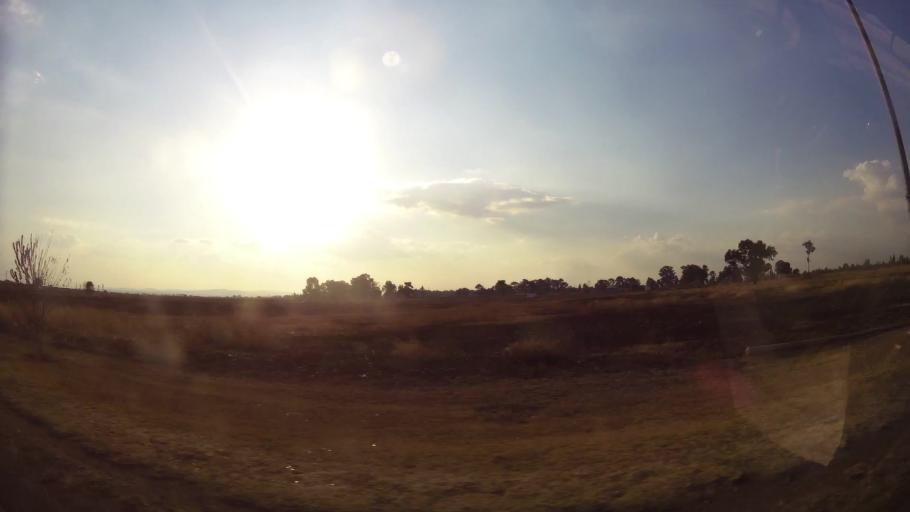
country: ZA
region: Gauteng
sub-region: Ekurhuleni Metropolitan Municipality
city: Germiston
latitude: -26.3394
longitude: 28.2244
